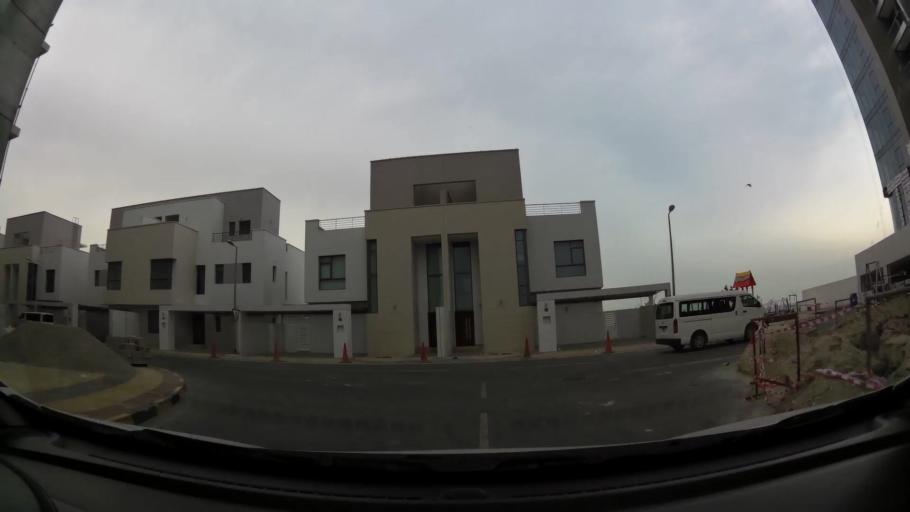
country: BH
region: Central Governorate
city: Dar Kulayb
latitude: 25.8687
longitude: 50.6099
